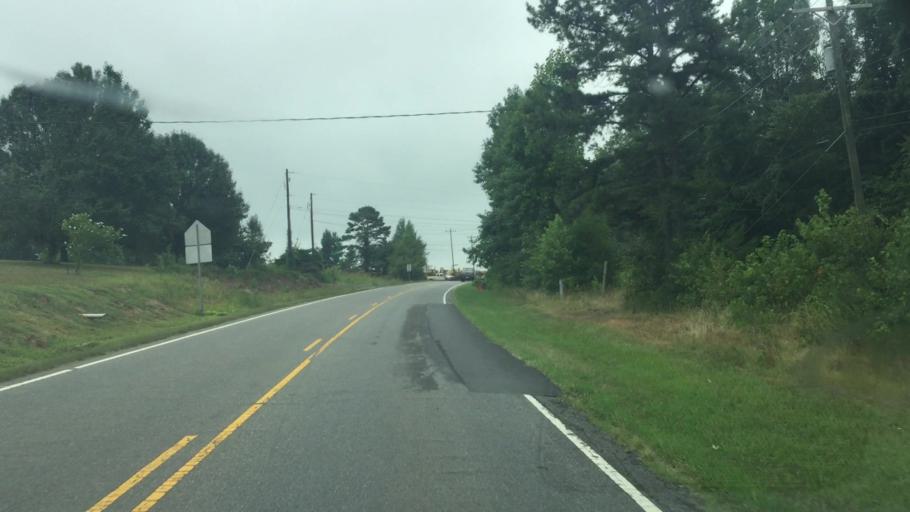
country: US
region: North Carolina
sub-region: Iredell County
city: Mooresville
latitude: 35.5531
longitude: -80.7776
